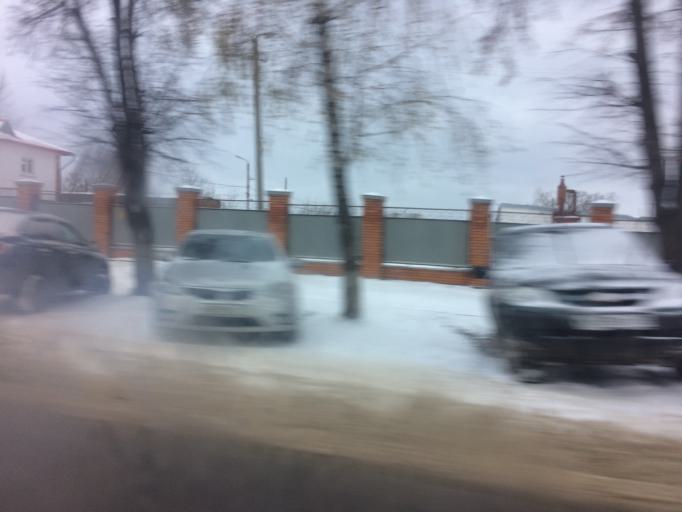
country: RU
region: Tula
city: Tula
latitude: 54.1648
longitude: 37.6400
